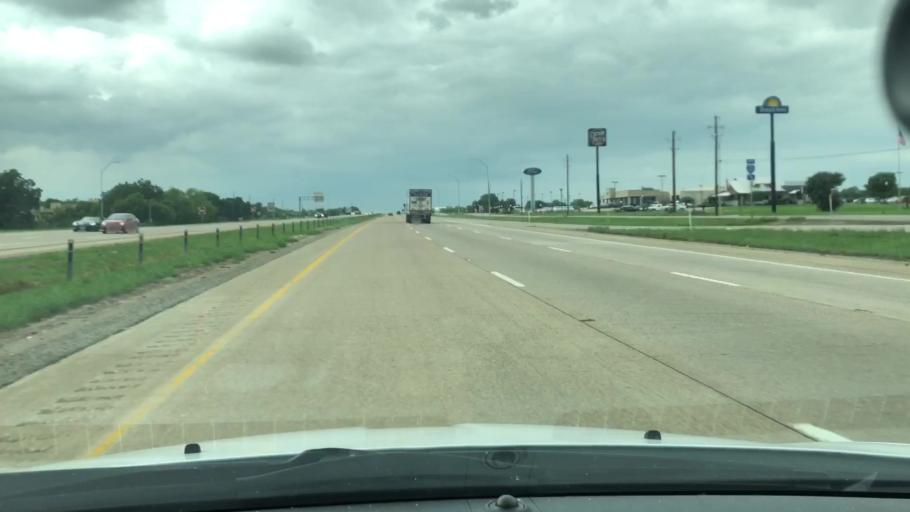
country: US
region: Texas
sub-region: Ellis County
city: Ennis
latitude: 32.3379
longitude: -96.6181
